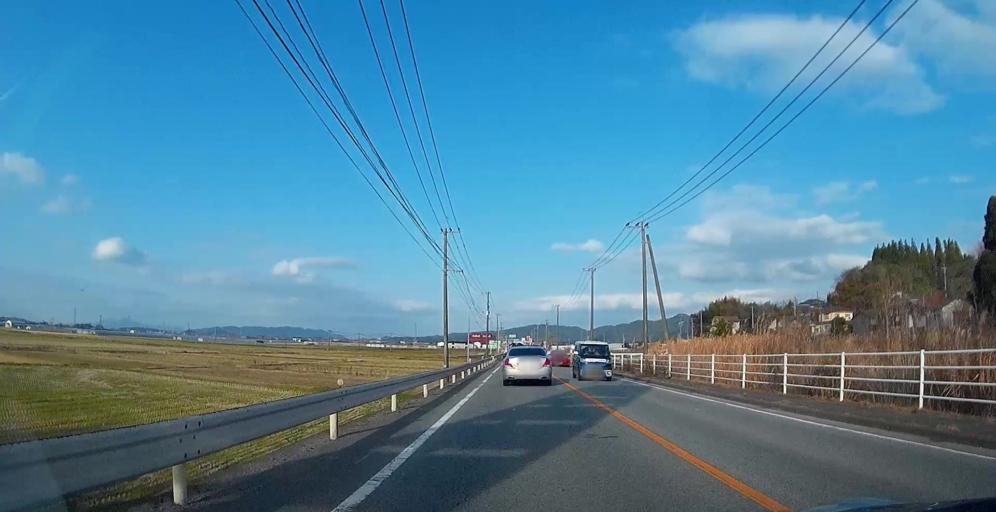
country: JP
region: Kumamoto
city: Matsubase
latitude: 32.5795
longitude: 130.6970
